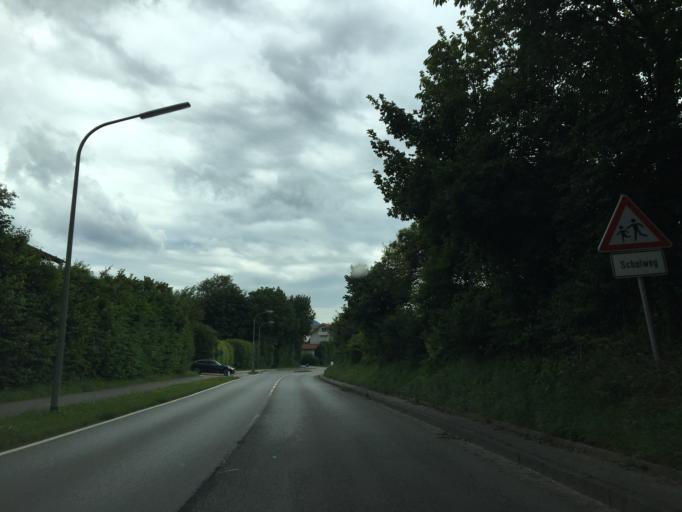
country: DE
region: Bavaria
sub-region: Upper Bavaria
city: Flintsbach
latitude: 47.7243
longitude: 12.1232
